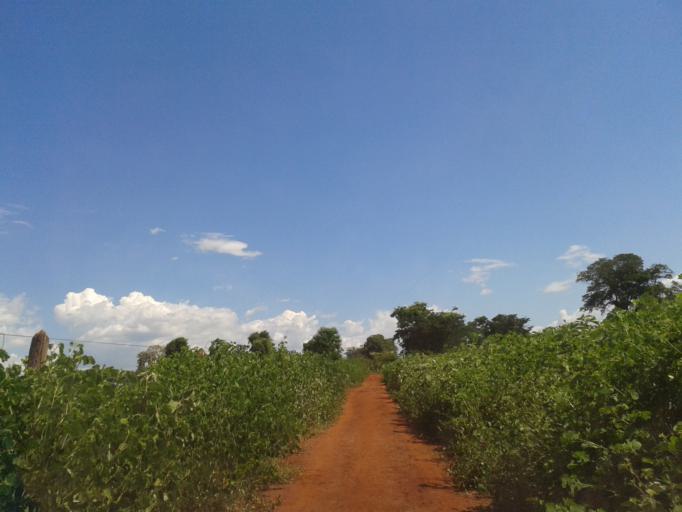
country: BR
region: Minas Gerais
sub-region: Santa Vitoria
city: Santa Vitoria
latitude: -19.1018
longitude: -50.5276
